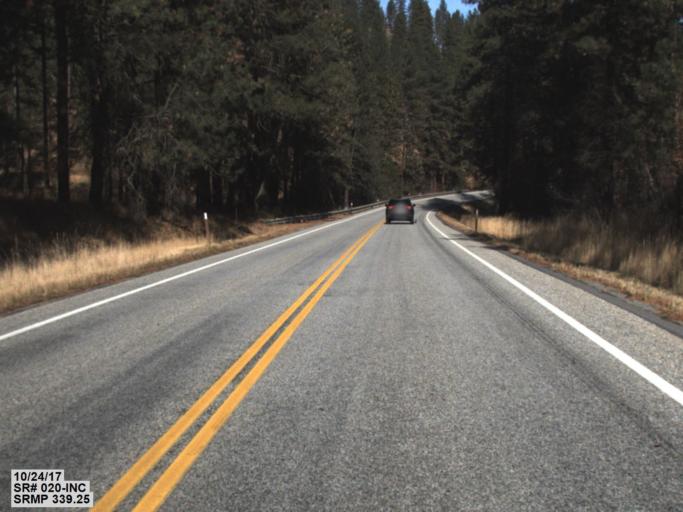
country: US
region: Washington
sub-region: Stevens County
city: Kettle Falls
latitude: 48.5924
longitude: -118.1472
